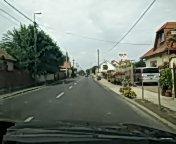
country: HU
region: Hajdu-Bihar
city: Debrecen
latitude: 47.5326
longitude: 21.6604
